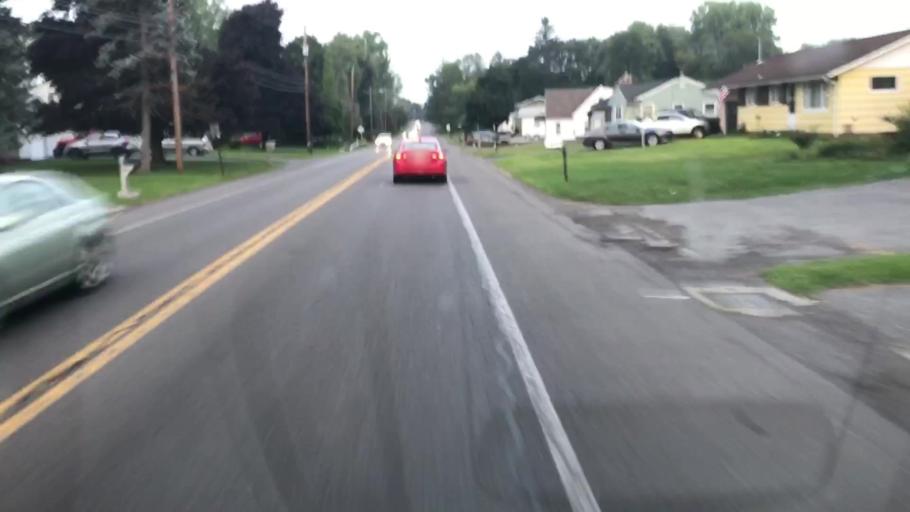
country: US
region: New York
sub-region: Onondaga County
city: North Syracuse
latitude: 43.1433
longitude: -76.1402
